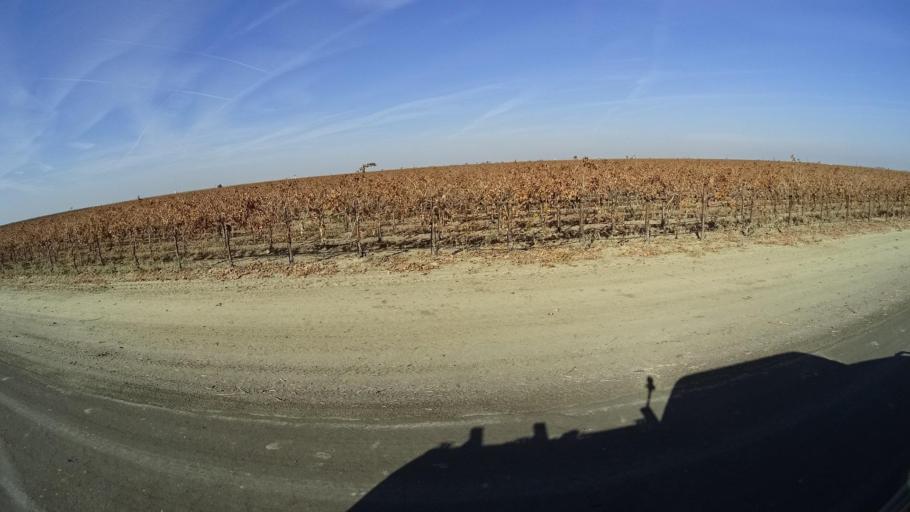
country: US
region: California
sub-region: Kern County
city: Wasco
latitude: 35.6887
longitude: -119.3877
